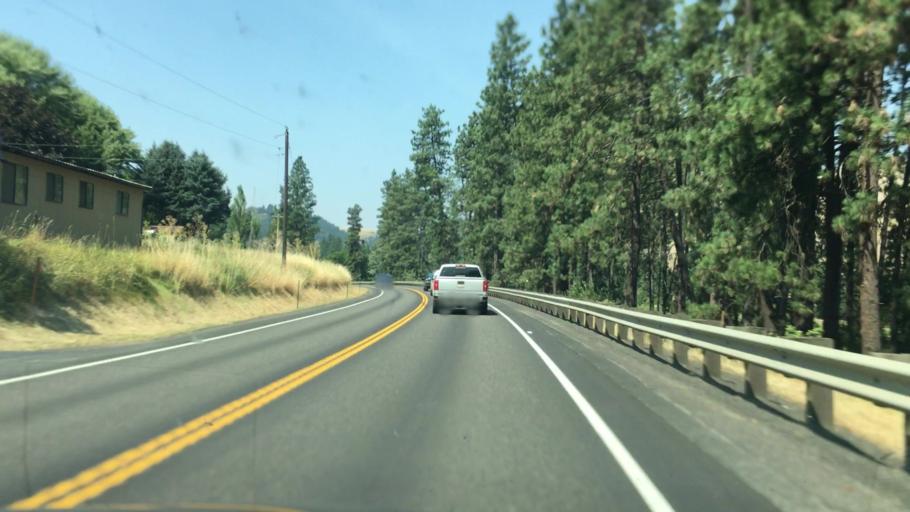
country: US
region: Idaho
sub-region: Clearwater County
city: Orofino
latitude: 46.5001
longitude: -116.4745
